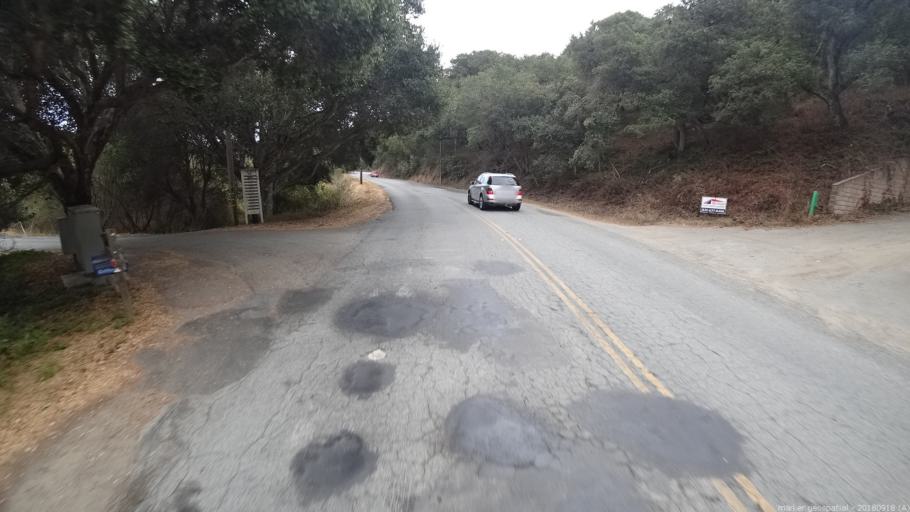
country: US
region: California
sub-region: Monterey County
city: Prunedale
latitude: 36.7782
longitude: -121.6468
